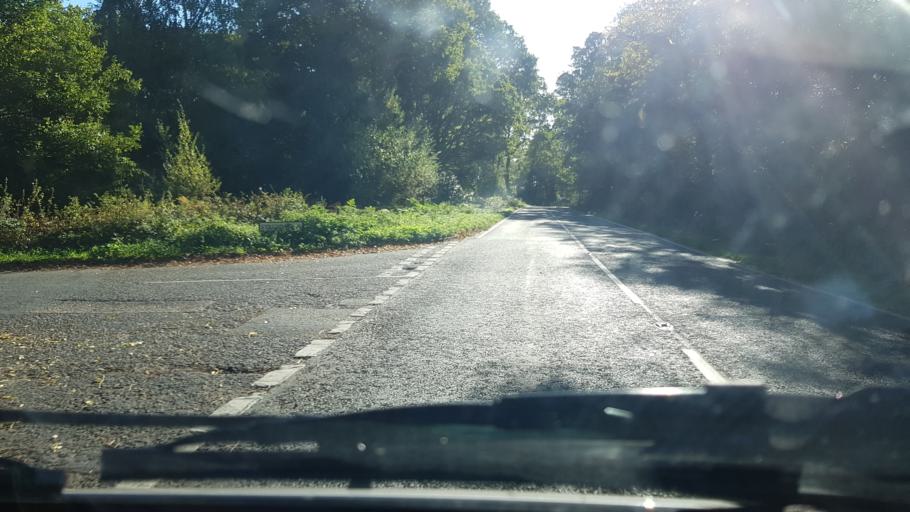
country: GB
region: England
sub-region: Surrey
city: Cranleigh
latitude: 51.1727
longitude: -0.5130
